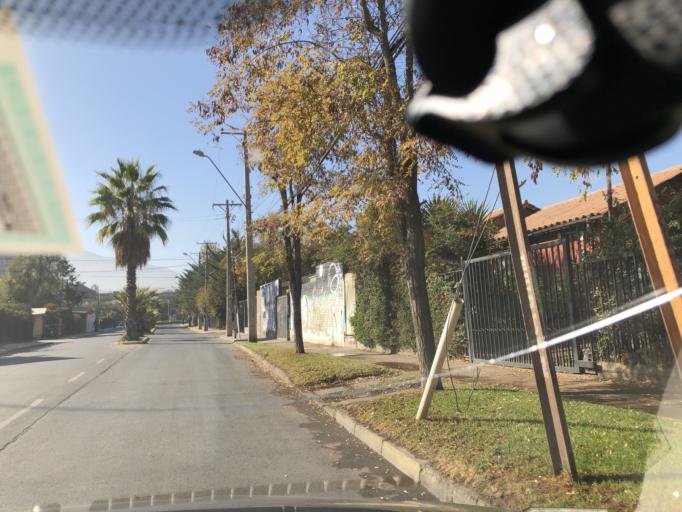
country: CL
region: Santiago Metropolitan
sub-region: Provincia de Cordillera
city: Puente Alto
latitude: -33.5840
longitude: -70.5828
